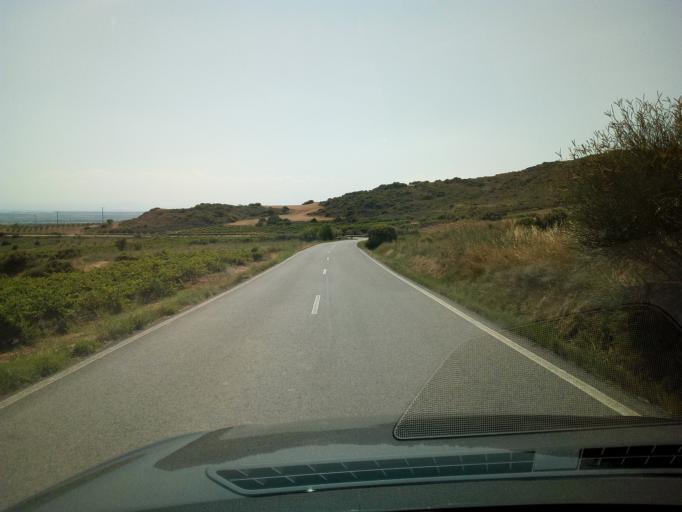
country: ES
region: Navarre
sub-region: Provincia de Navarra
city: San Martin de Unx
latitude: 42.5052
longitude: -1.5752
